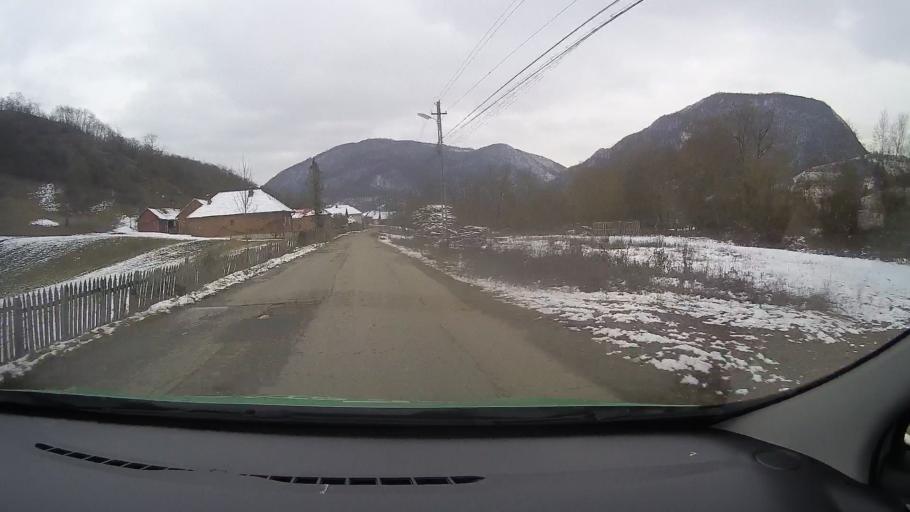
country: RO
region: Hunedoara
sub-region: Comuna Balsa
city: Balsa
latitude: 46.0247
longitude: 23.1132
